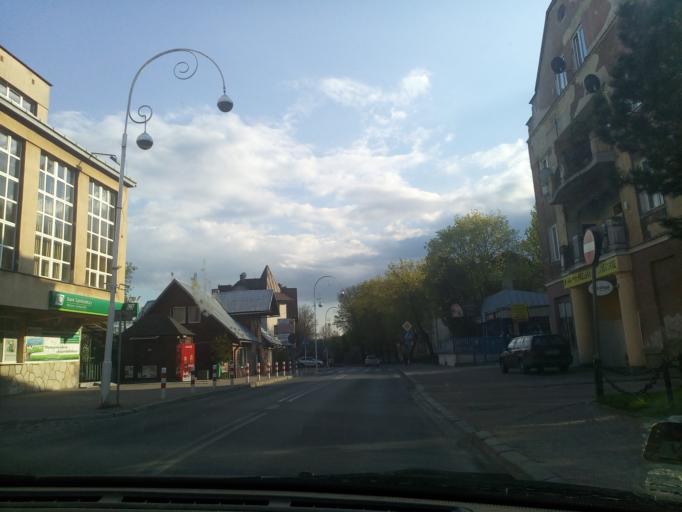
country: PL
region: Lesser Poland Voivodeship
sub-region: Powiat nowosadecki
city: Krynica-Zdroj
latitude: 49.4112
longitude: 20.9555
